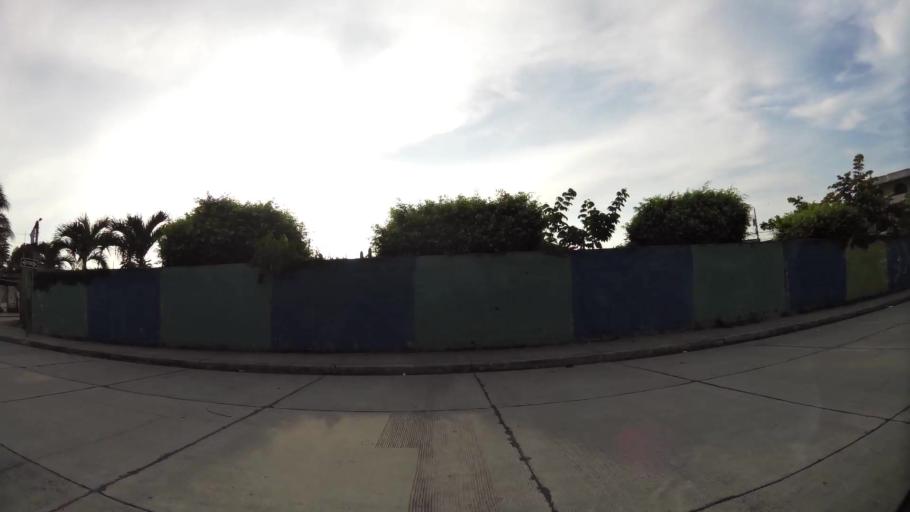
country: EC
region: Guayas
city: Eloy Alfaro
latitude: -2.0914
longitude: -79.8973
